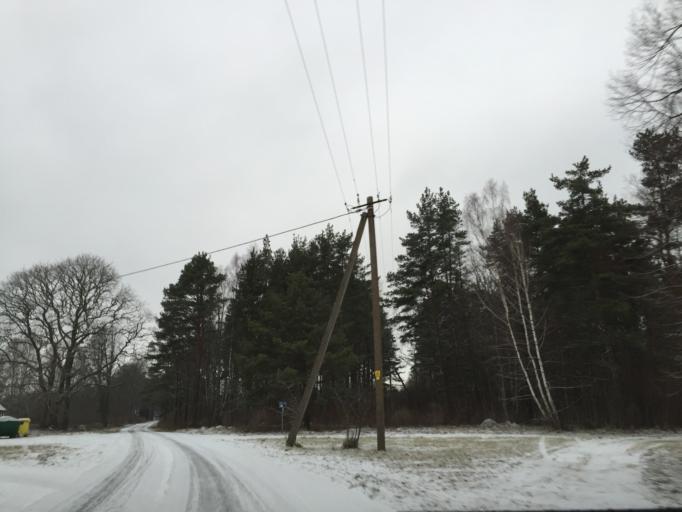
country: EE
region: Saare
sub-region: Orissaare vald
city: Orissaare
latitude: 58.6192
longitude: 23.1852
